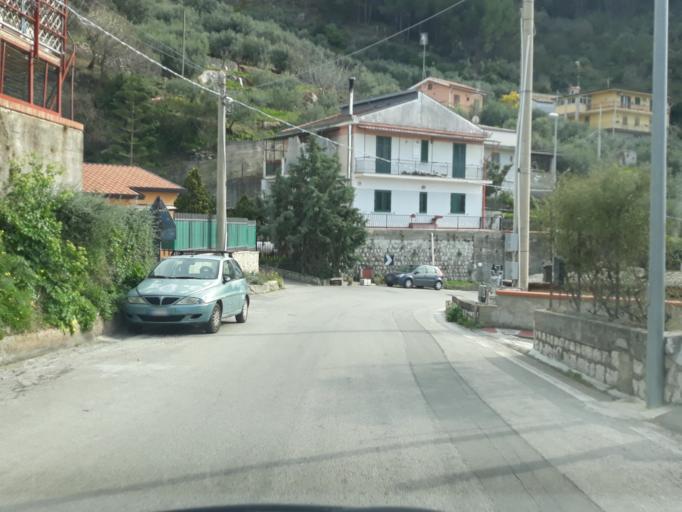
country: IT
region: Sicily
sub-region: Palermo
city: Altofonte
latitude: 38.0418
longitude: 13.3017
